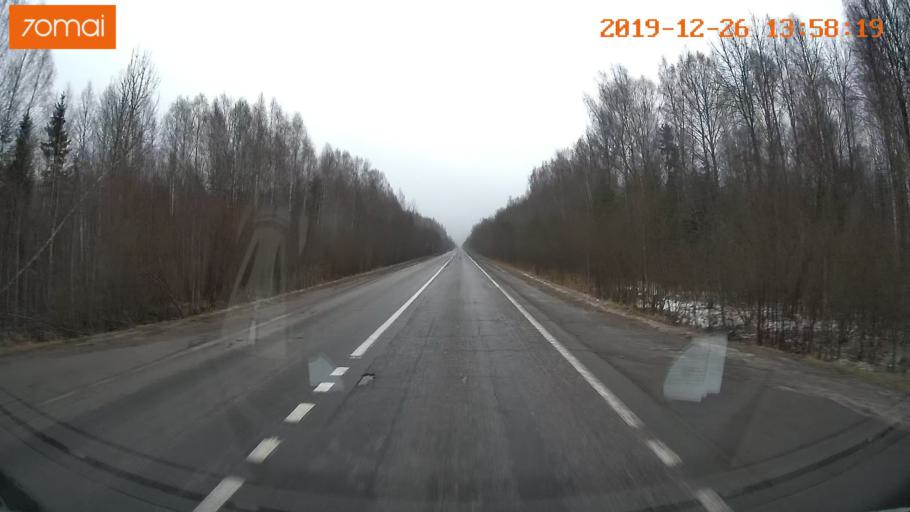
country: RU
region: Jaroslavl
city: Poshekhon'ye
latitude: 58.5751
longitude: 38.6982
